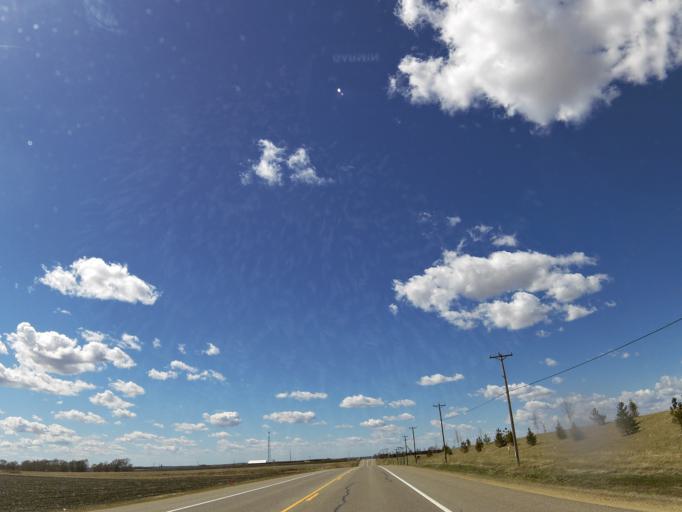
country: US
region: Minnesota
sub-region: Dakota County
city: Rosemount
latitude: 44.7175
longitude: -93.1068
